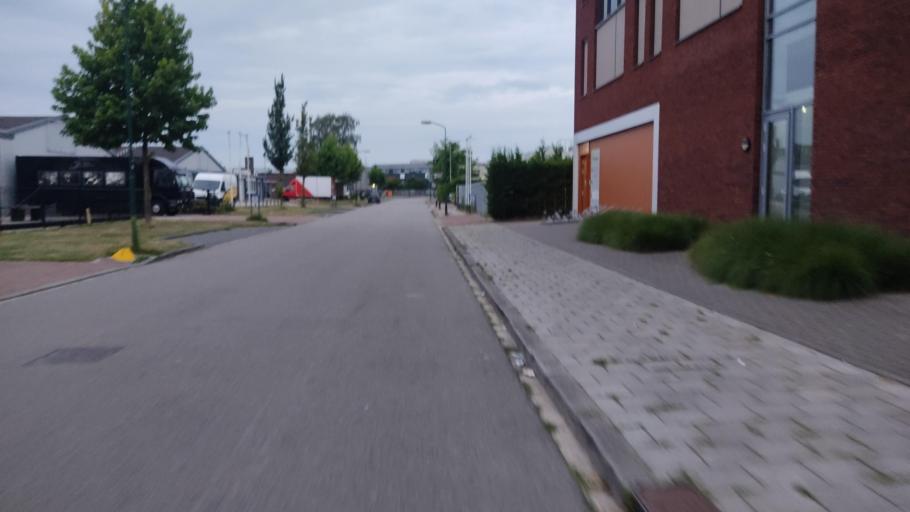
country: NL
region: Utrecht
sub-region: Gemeente Veenendaal
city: Veenendaal
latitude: 52.0166
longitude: 5.5575
